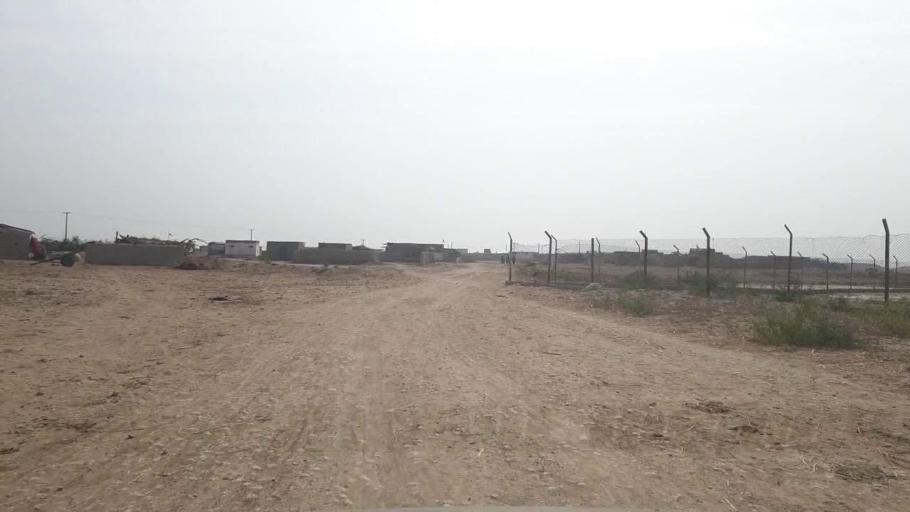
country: PK
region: Sindh
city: Tando Muhammad Khan
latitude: 25.1596
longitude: 68.4702
